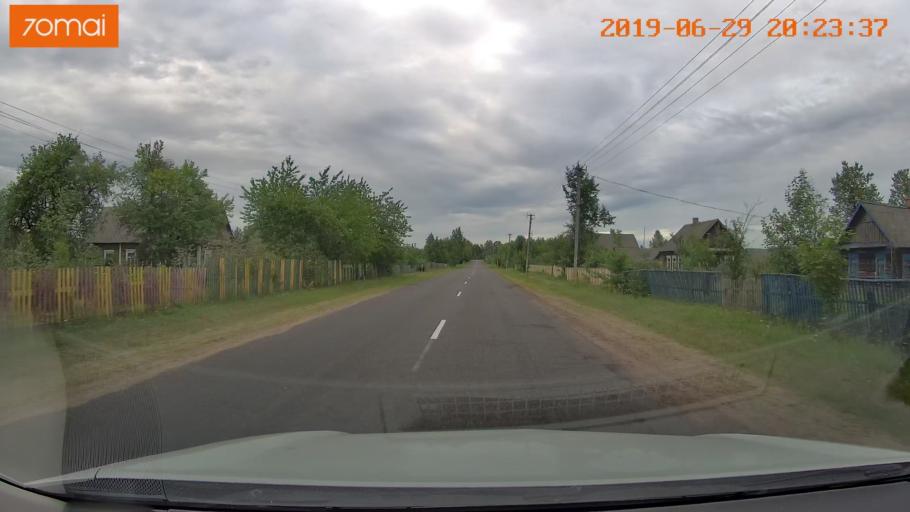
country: BY
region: Brest
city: Asnyezhytsy
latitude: 52.4467
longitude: 26.2617
